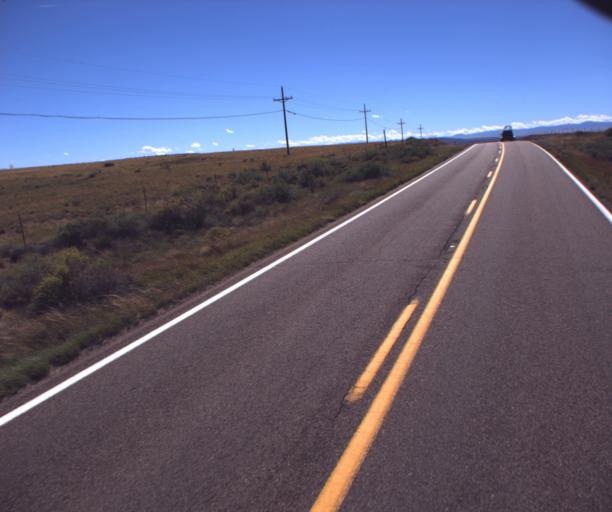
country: US
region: Arizona
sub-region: Apache County
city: Saint Johns
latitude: 34.5611
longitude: -109.3416
